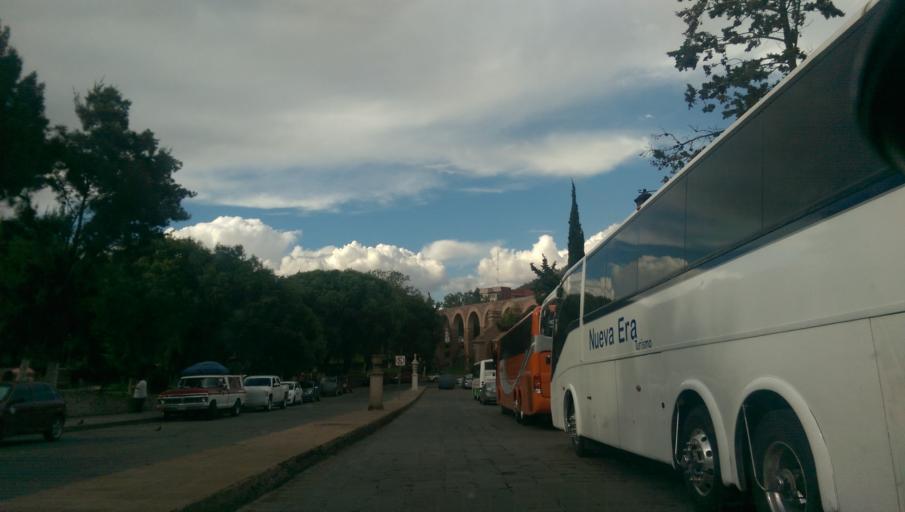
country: MX
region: Zacatecas
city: Zacatecas
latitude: 22.7686
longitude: -102.5766
